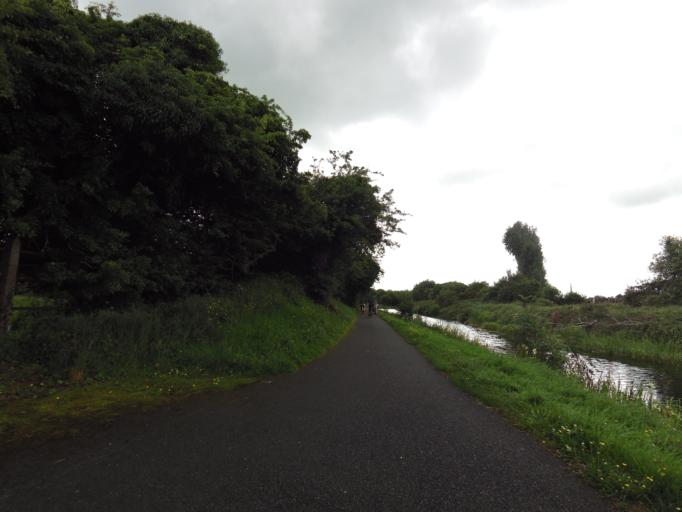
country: IE
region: Leinster
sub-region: An Iarmhi
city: An Muileann gCearr
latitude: 53.5098
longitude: -7.4004
